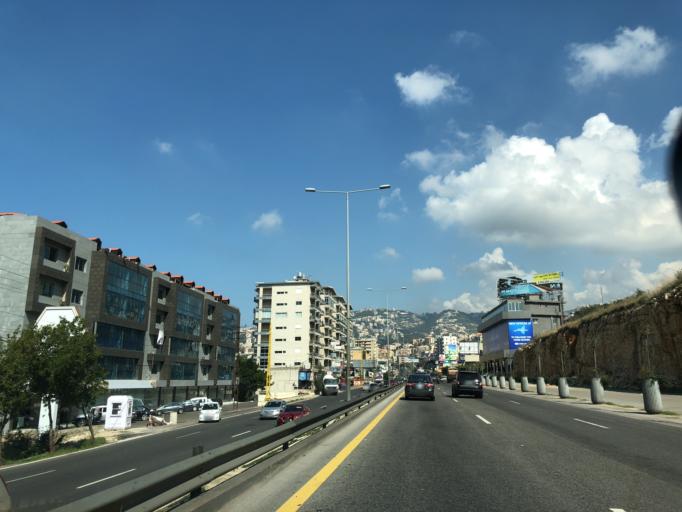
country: LB
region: Mont-Liban
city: Djounie
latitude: 33.9981
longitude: 35.6463
